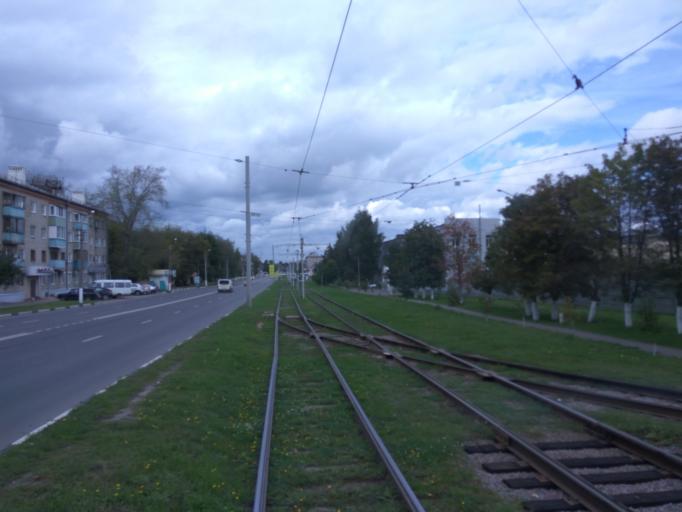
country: RU
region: Moskovskaya
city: Kolomna
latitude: 55.0881
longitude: 38.7659
